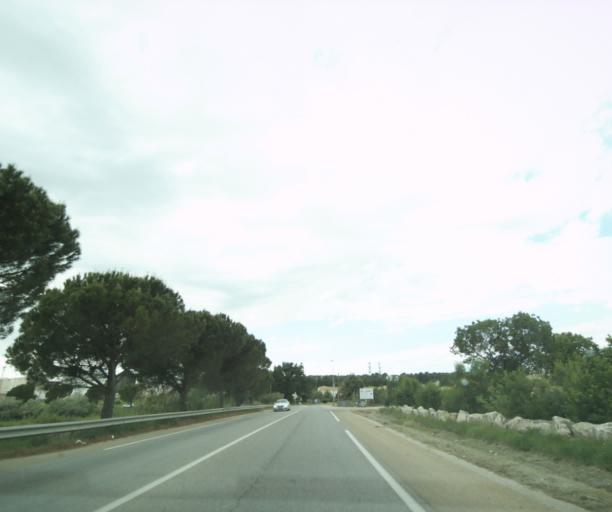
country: FR
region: Provence-Alpes-Cote d'Azur
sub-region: Departement des Bouches-du-Rhone
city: Rognac
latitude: 43.5033
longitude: 5.2219
